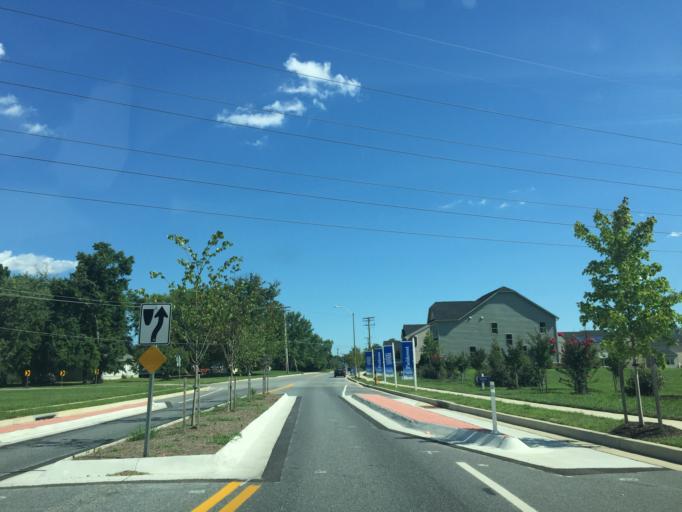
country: US
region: Maryland
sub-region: Baltimore County
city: White Marsh
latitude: 39.4035
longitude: -76.4092
